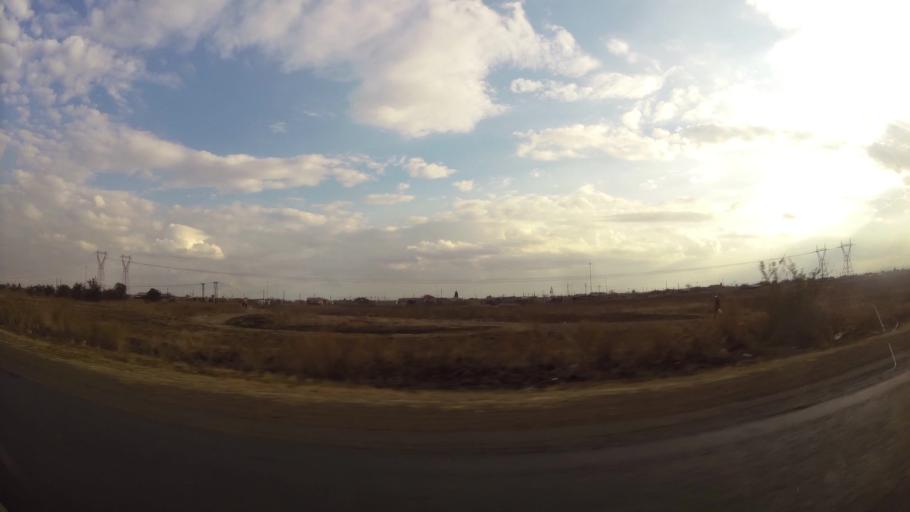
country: ZA
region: Gauteng
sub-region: Sedibeng District Municipality
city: Vanderbijlpark
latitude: -26.6822
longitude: 27.7971
